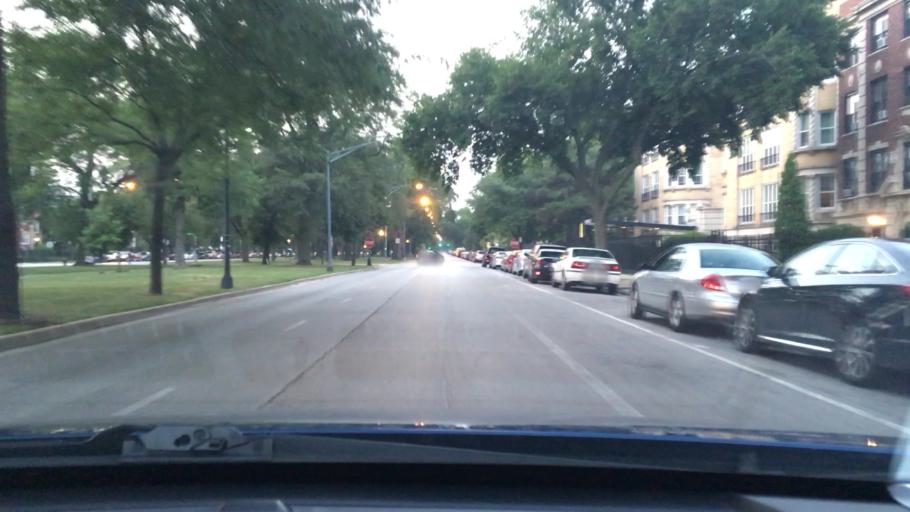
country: US
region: Illinois
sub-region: Cook County
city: Chicago
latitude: 41.8051
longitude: -87.6038
